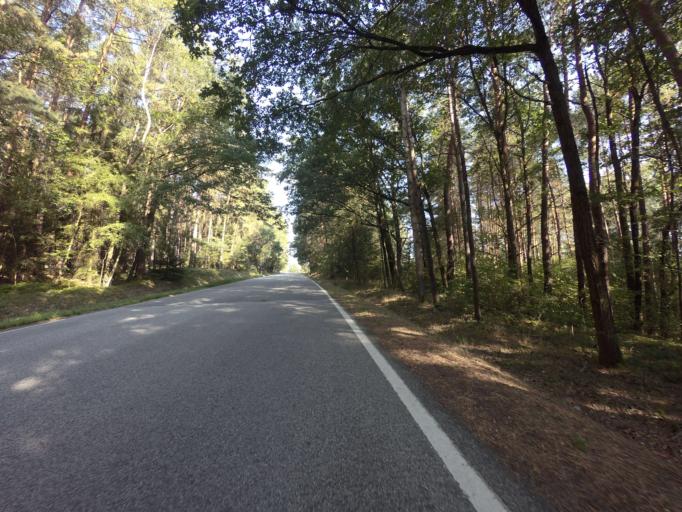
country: CZ
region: Jihocesky
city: Tyn nad Vltavou
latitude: 49.2685
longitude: 14.4095
